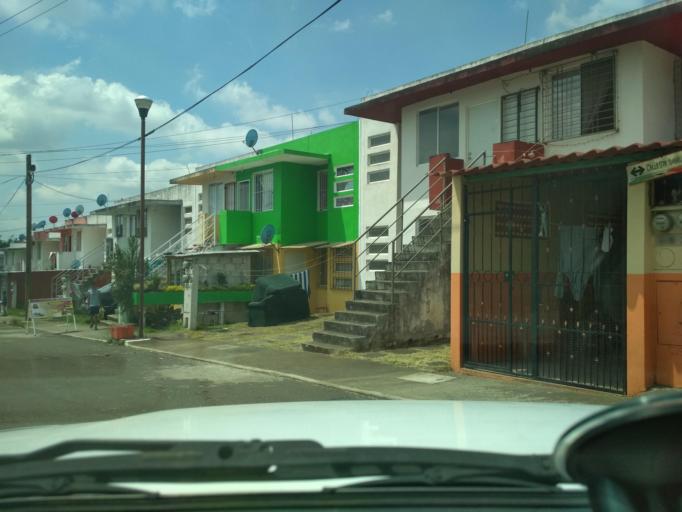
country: MX
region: Veracruz
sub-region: Fortin
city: Fraccionamiento los Alamos
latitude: 18.9309
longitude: -96.9763
